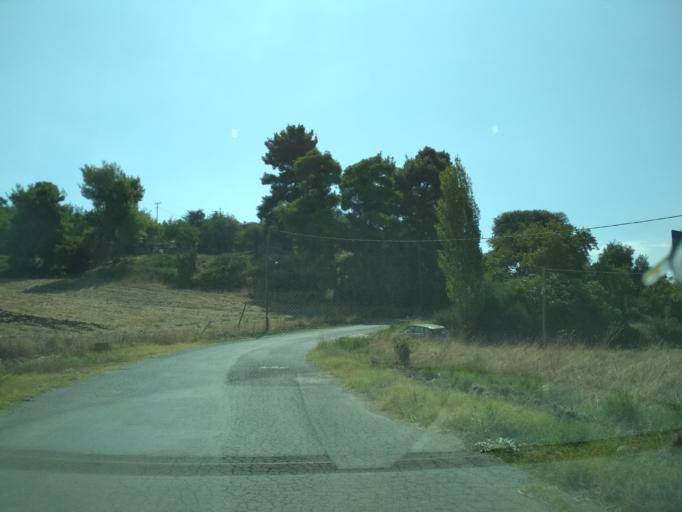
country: GR
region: Central Greece
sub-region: Nomos Evvoias
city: Roviai
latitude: 38.8198
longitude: 23.2681
